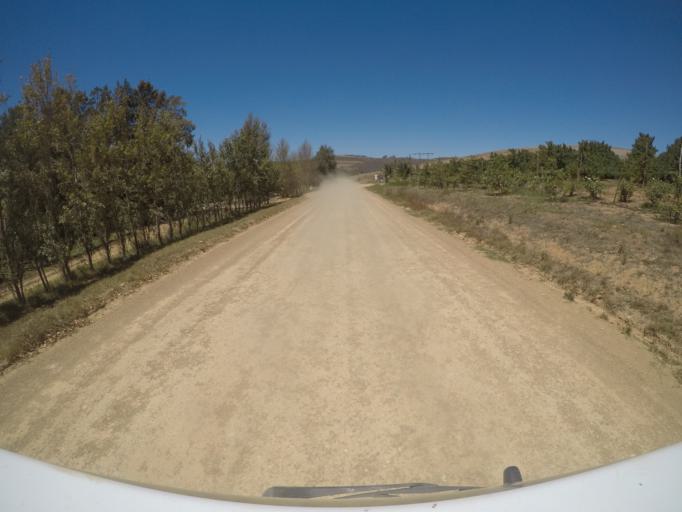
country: ZA
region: Western Cape
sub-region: Overberg District Municipality
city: Grabouw
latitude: -34.1101
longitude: 19.2134
